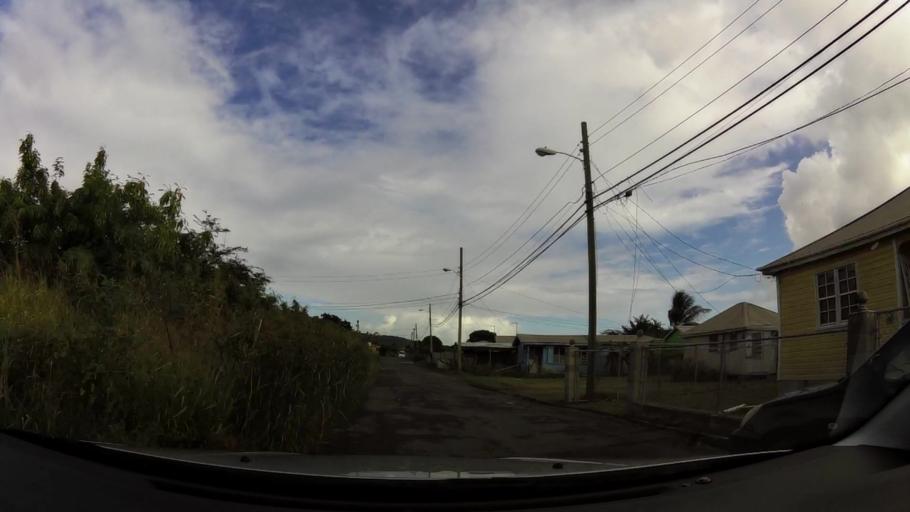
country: AG
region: Saint George
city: Piggotts
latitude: 17.1234
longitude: -61.8227
